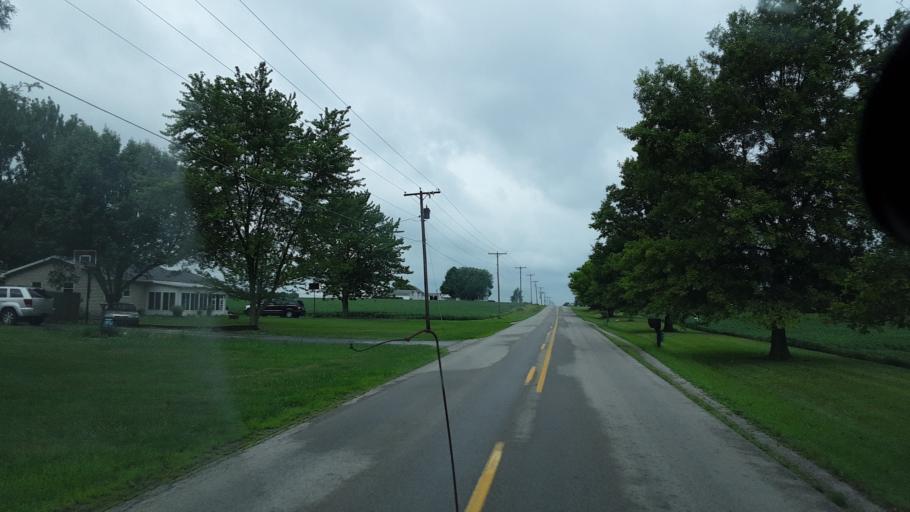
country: US
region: Indiana
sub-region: Allen County
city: New Haven
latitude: 40.9473
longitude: -85.0246
